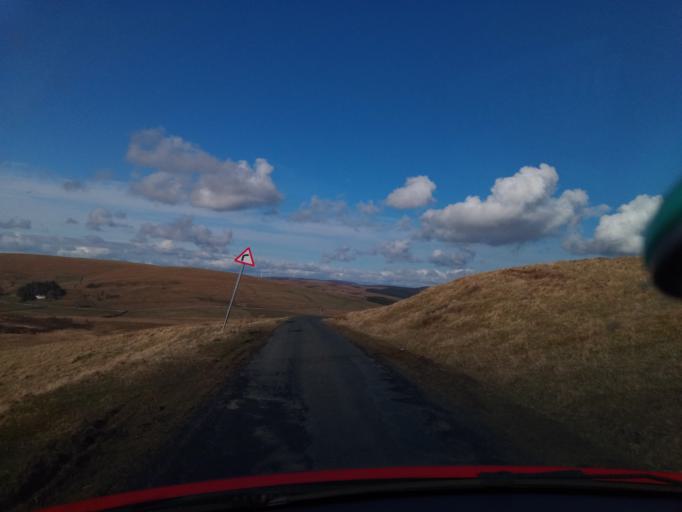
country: GB
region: Scotland
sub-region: The Scottish Borders
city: Hawick
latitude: 55.4462
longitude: -2.8875
